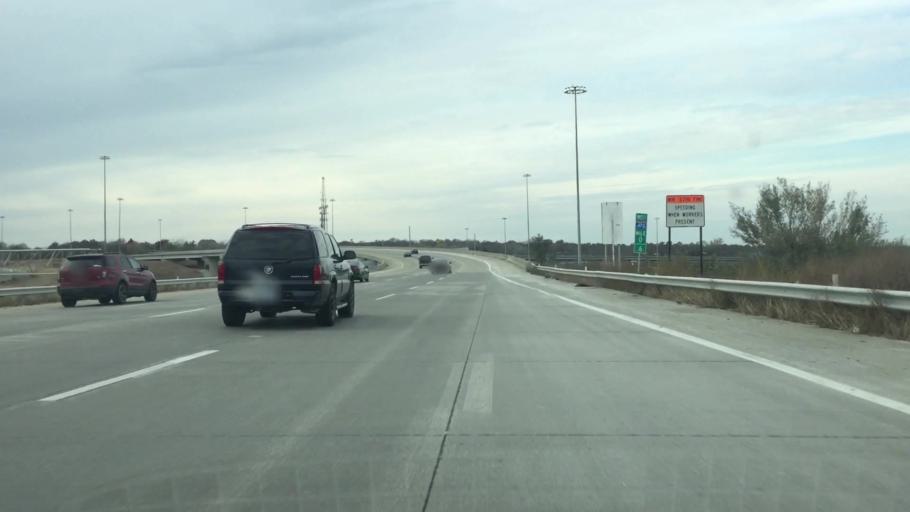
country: US
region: Missouri
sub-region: Jackson County
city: Grandview
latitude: 38.9367
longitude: -94.5324
